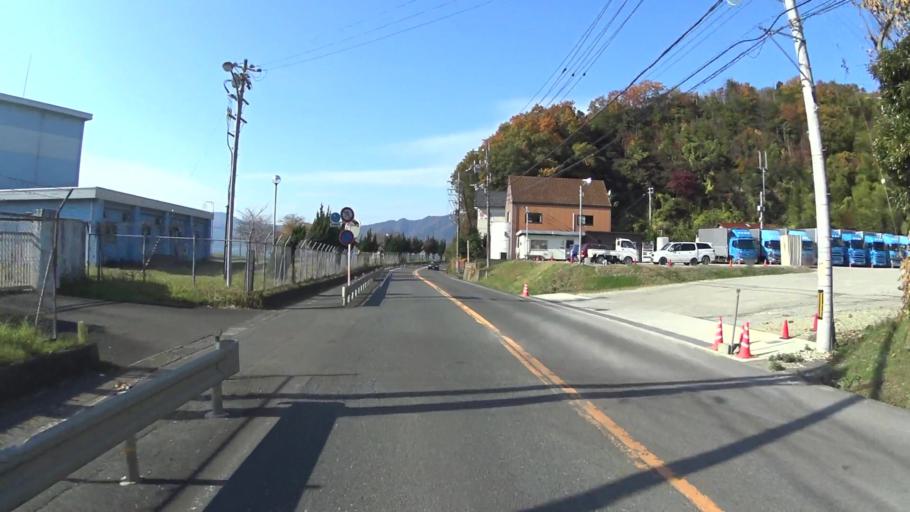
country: JP
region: Kyoto
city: Maizuru
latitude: 35.4870
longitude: 135.3977
